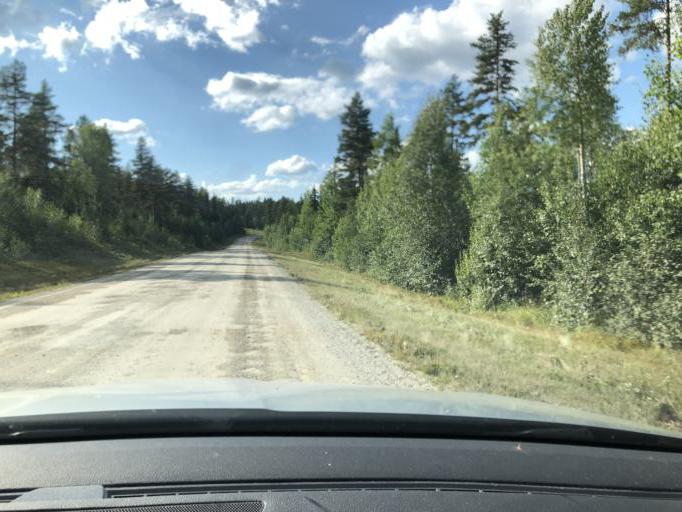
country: SE
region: Vaesternorrland
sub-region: Solleftea Kommun
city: Solleftea
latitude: 63.3133
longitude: 17.2570
